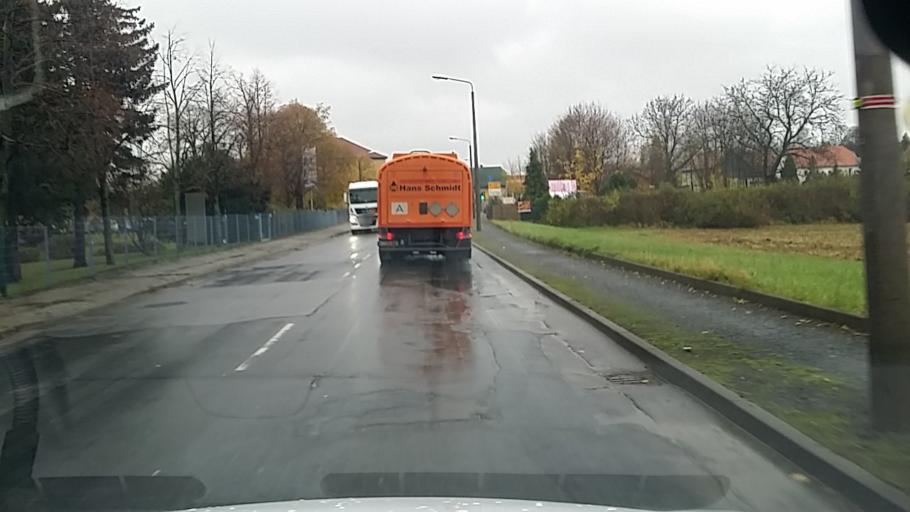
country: DE
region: Saxony
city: Dohna
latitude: 50.9904
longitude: 13.8100
